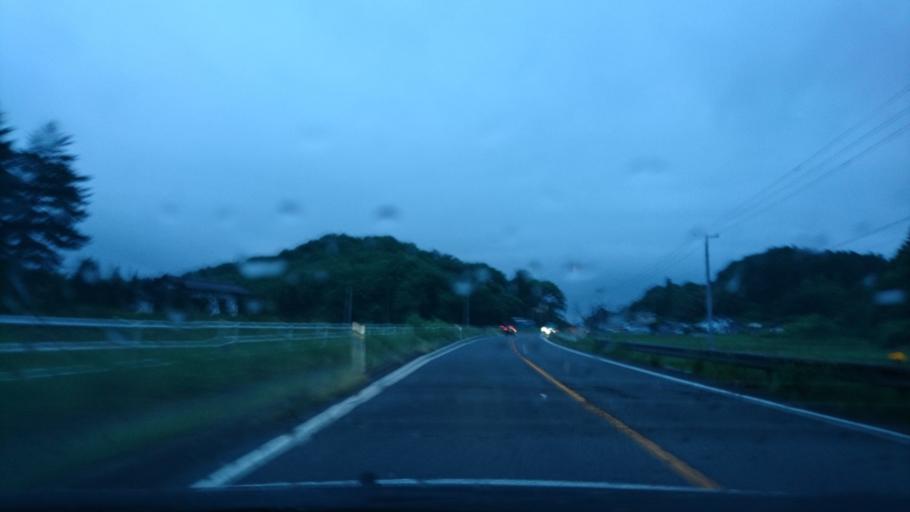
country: JP
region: Iwate
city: Ichinoseki
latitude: 38.7863
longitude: 141.0500
